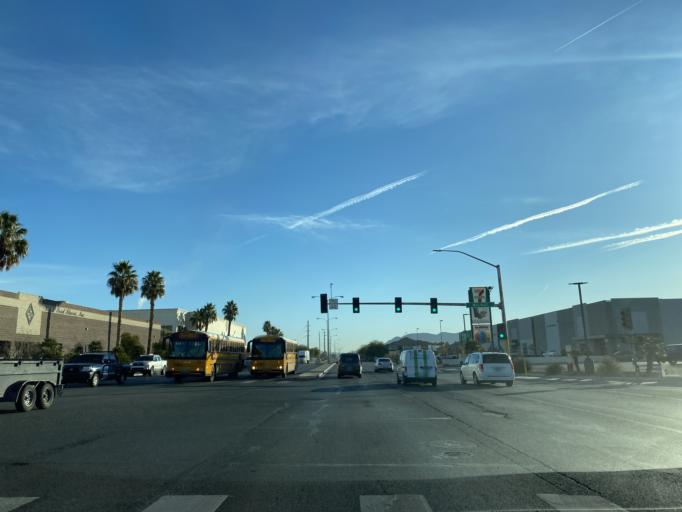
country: US
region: Nevada
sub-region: Clark County
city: Nellis Air Force Base
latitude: 36.2403
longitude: -115.0894
